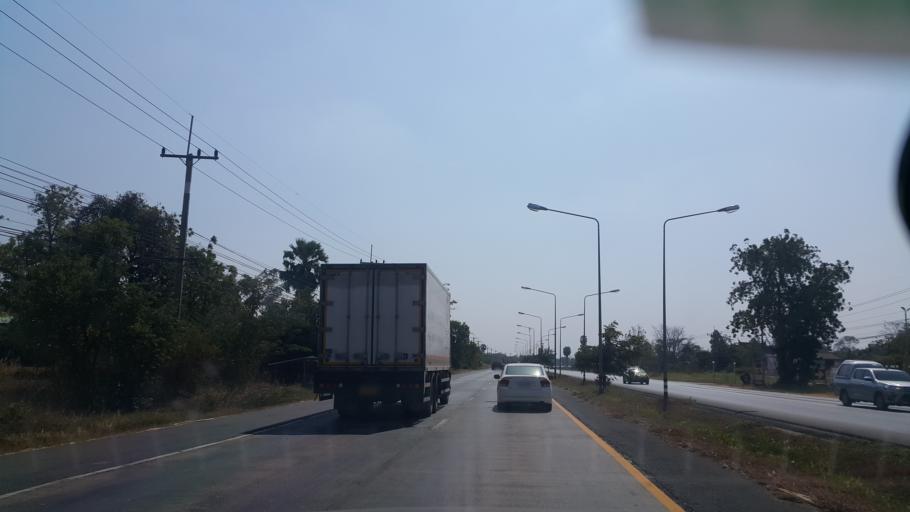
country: TH
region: Nakhon Ratchasima
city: Sida
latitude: 15.5280
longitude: 102.5433
